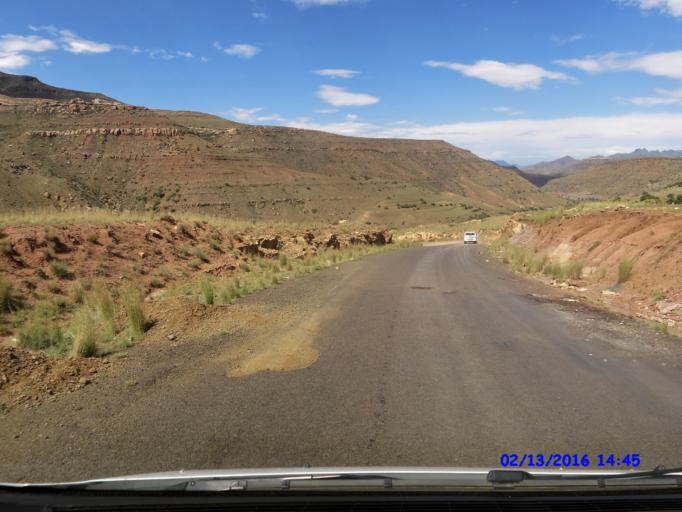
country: LS
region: Qacha's Nek
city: Qacha's Nek
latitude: -30.0638
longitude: 28.3997
